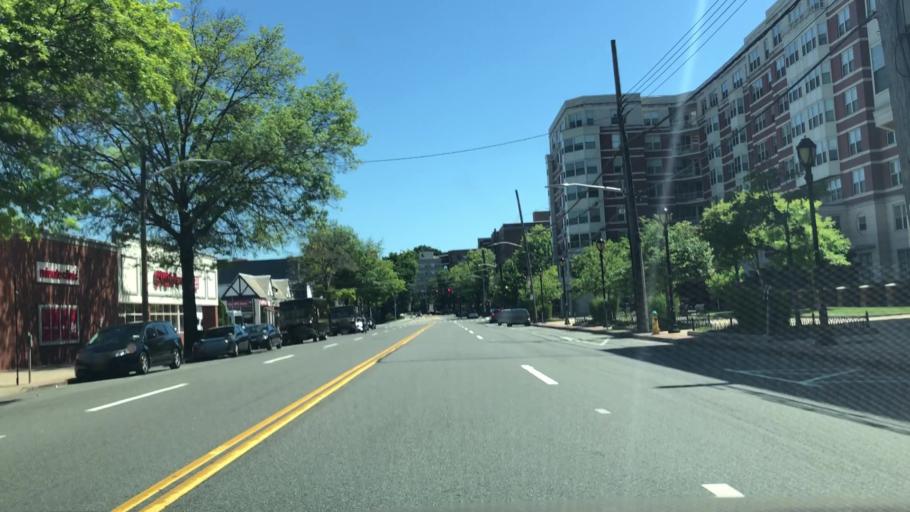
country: US
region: New York
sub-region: Westchester County
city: White Plains
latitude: 41.0255
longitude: -73.7636
